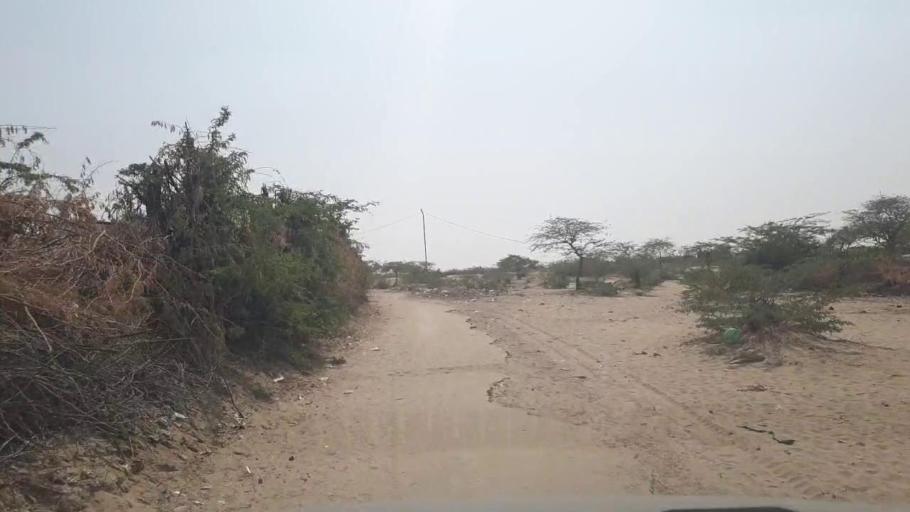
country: PK
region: Sindh
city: Chor
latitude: 25.4724
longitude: 69.7829
